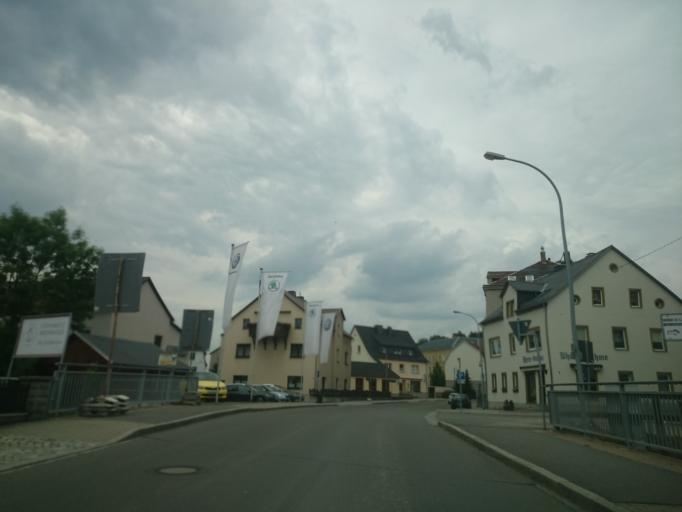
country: DE
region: Saxony
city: Eppendorf
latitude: 50.7976
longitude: 13.2282
